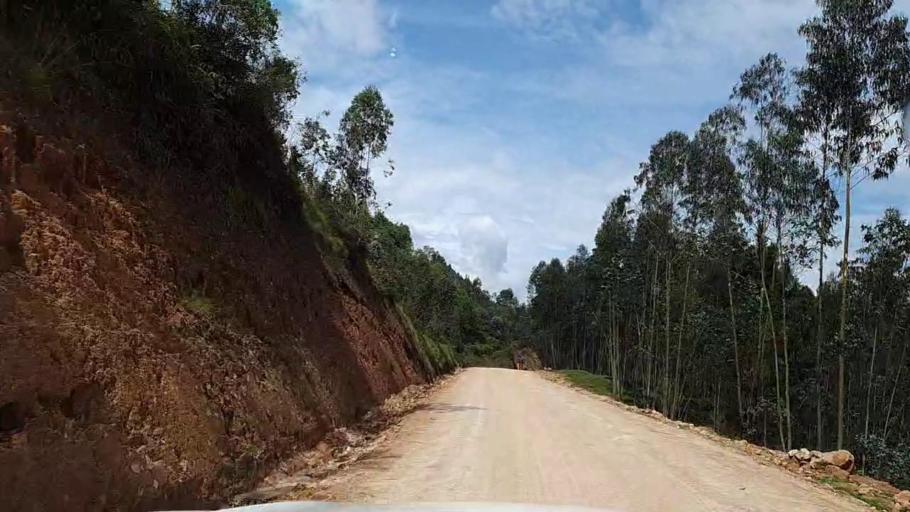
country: RW
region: Southern Province
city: Nzega
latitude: -2.3409
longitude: 29.4374
